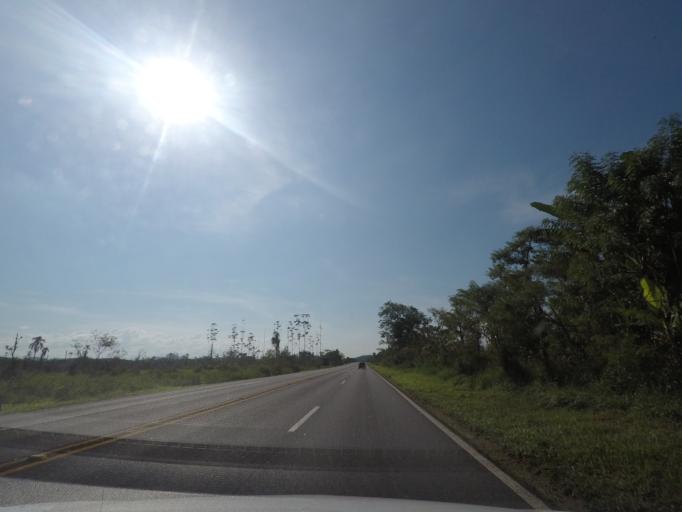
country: BR
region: Parana
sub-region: Paranagua
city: Paranagua
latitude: -25.5851
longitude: -48.6119
